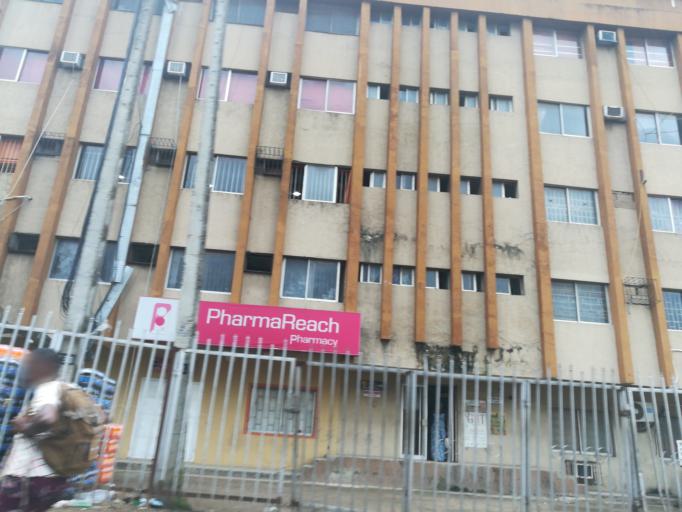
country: NG
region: Lagos
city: Ikeja
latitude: 6.5961
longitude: 3.3362
